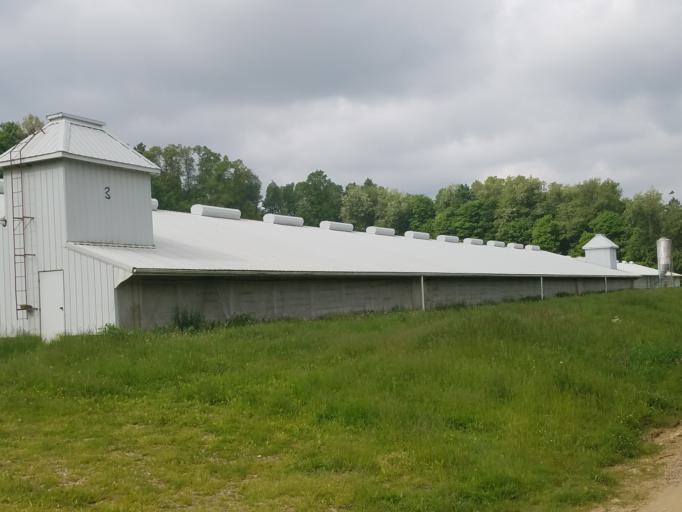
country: US
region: Ohio
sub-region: Knox County
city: Danville
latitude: 40.5481
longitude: -82.3699
